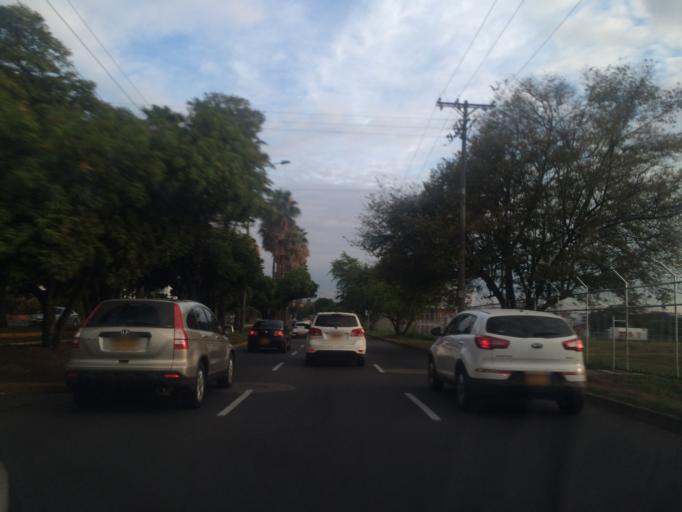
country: CO
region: Valle del Cauca
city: Cali
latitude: 3.3769
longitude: -76.5372
